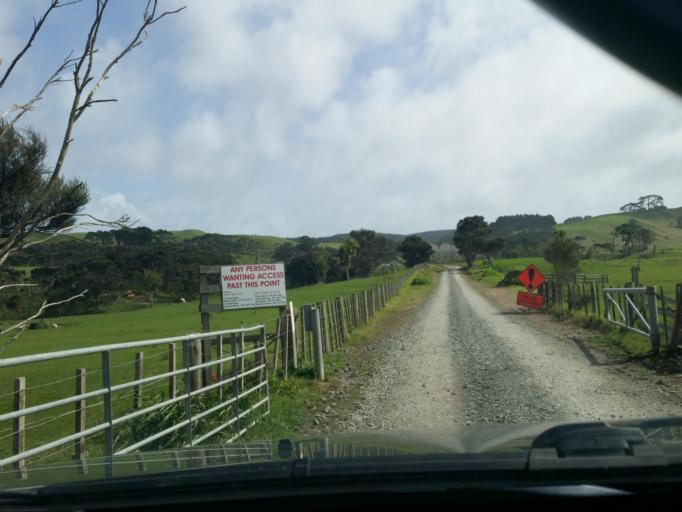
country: NZ
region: Auckland
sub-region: Auckland
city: Wellsford
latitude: -36.2963
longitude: 174.1026
